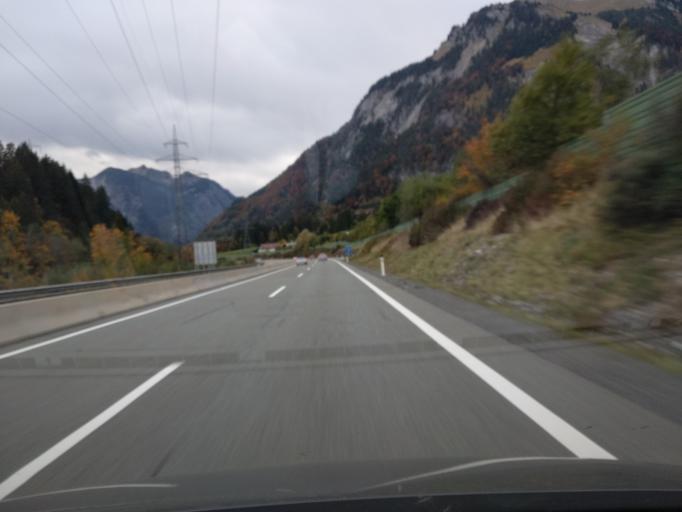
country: AT
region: Vorarlberg
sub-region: Politischer Bezirk Bludenz
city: Dalaas
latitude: 47.1278
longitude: 10.0366
